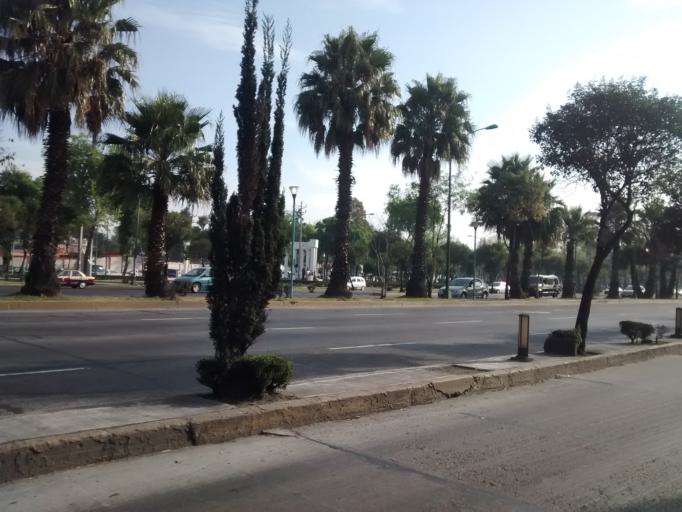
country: MX
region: Mexico City
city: Mexico City
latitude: 19.4217
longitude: -99.1193
